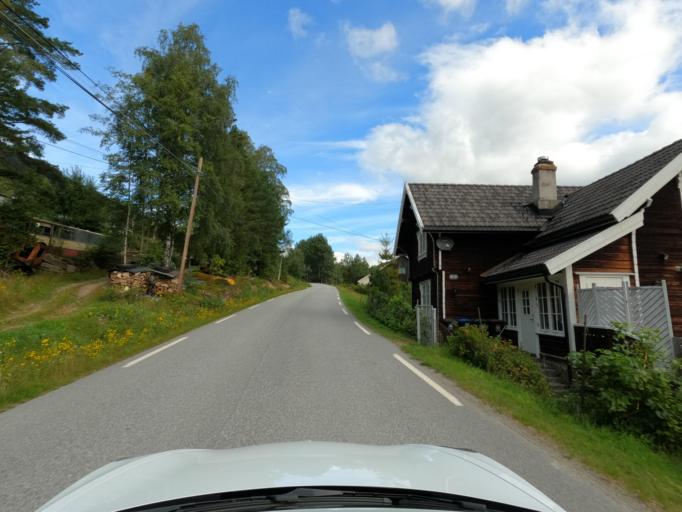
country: NO
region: Telemark
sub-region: Tinn
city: Rjukan
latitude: 60.0049
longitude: 8.7456
